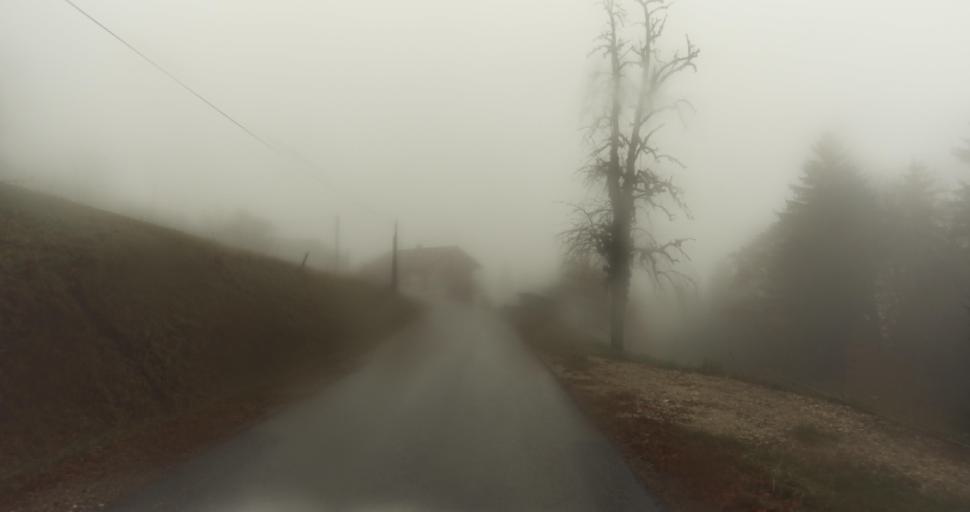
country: FR
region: Rhone-Alpes
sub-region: Departement de la Haute-Savoie
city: Villaz
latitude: 45.9754
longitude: 6.2122
